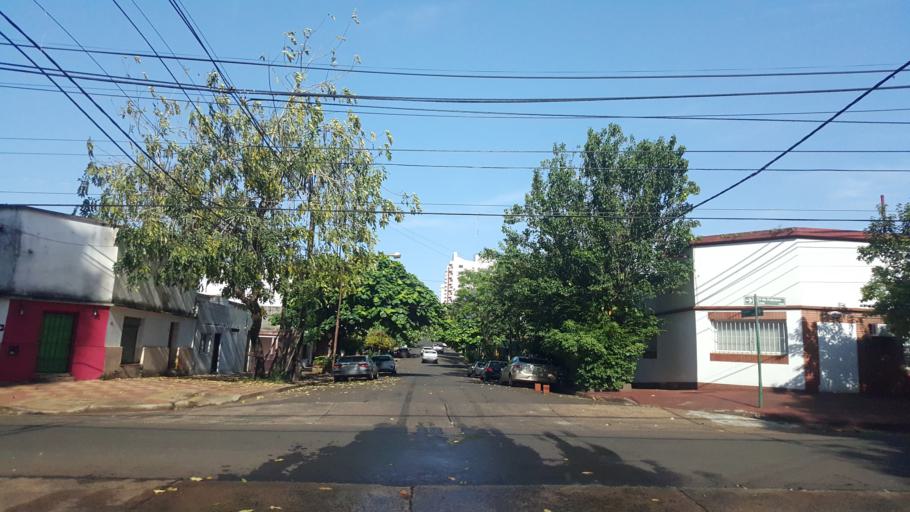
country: AR
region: Misiones
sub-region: Departamento de Capital
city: Posadas
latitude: -27.3730
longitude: -55.8911
